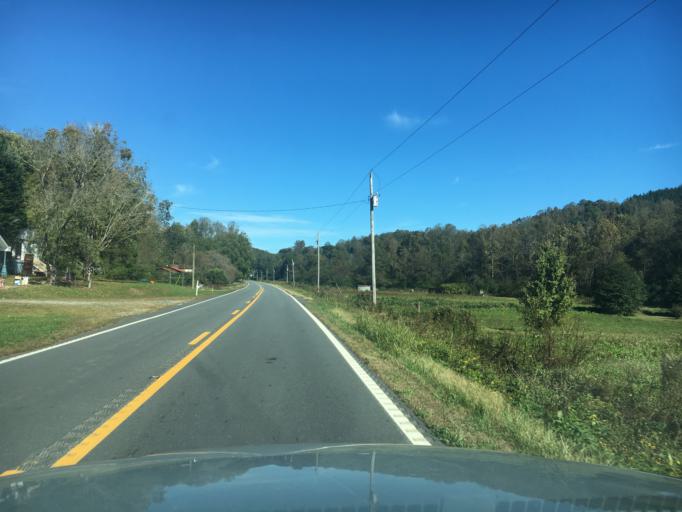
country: US
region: North Carolina
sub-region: Burke County
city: Glen Alpine
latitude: 35.5490
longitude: -81.8552
